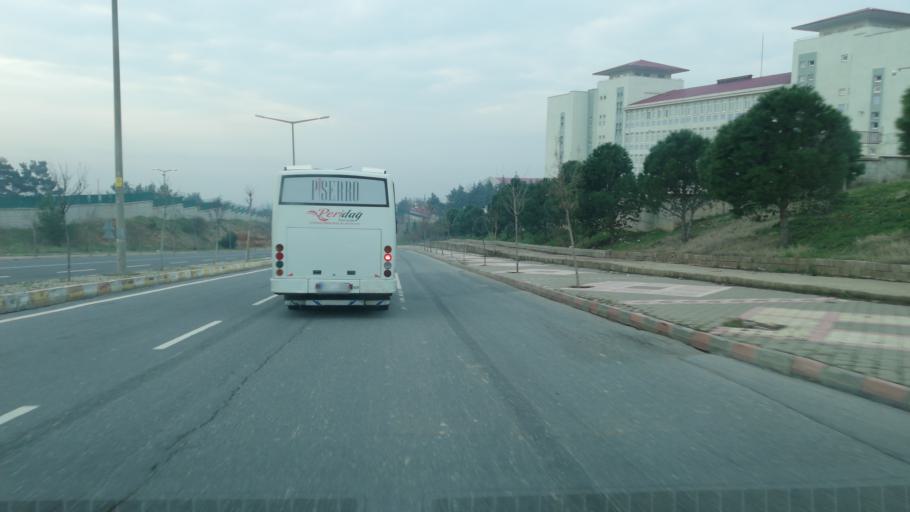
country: TR
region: Kahramanmaras
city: Kahramanmaras
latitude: 37.5985
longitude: 36.9253
